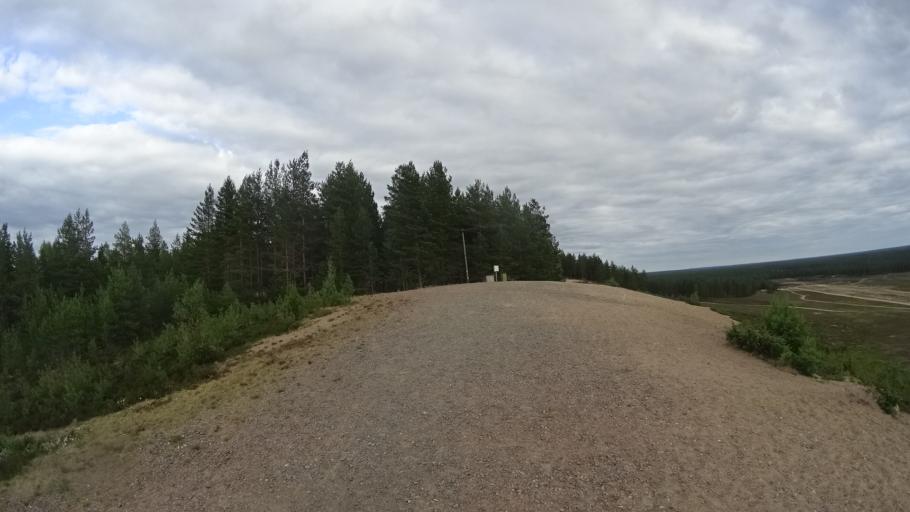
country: FI
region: Satakunta
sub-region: Pohjois-Satakunta
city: Jaemijaervi
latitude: 61.7767
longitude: 22.7189
